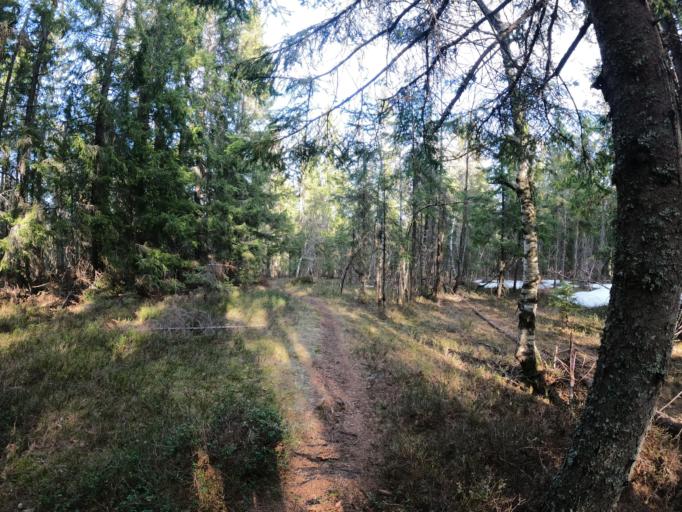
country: NO
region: Akershus
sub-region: Nannestad
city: Teigebyen
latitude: 60.2444
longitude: 10.9364
